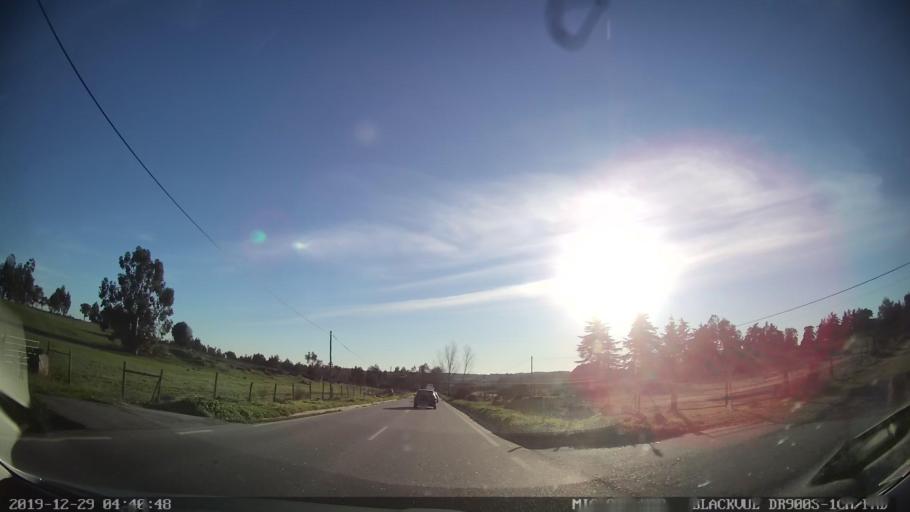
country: PT
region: Guarda
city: Alcains
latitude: 39.9221
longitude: -7.4104
